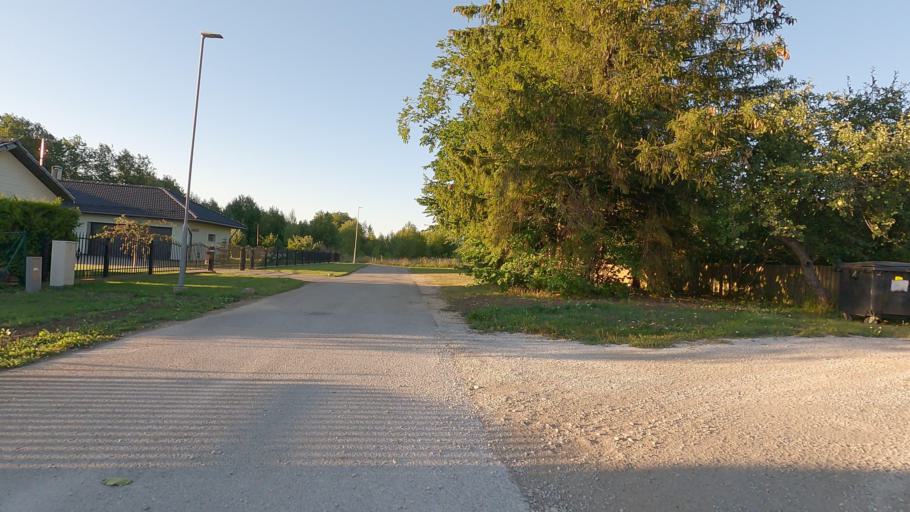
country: EE
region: Raplamaa
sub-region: Rapla vald
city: Rapla
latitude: 59.0049
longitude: 24.7812
